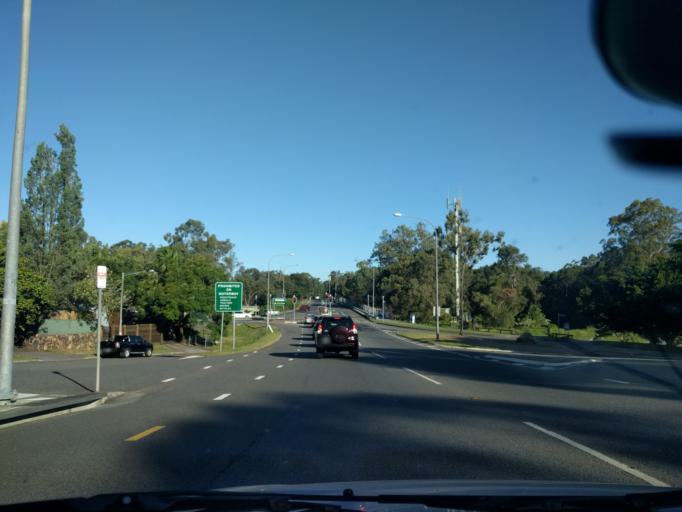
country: AU
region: Queensland
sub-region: Brisbane
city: Kenmore Hills
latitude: -27.5151
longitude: 152.9543
